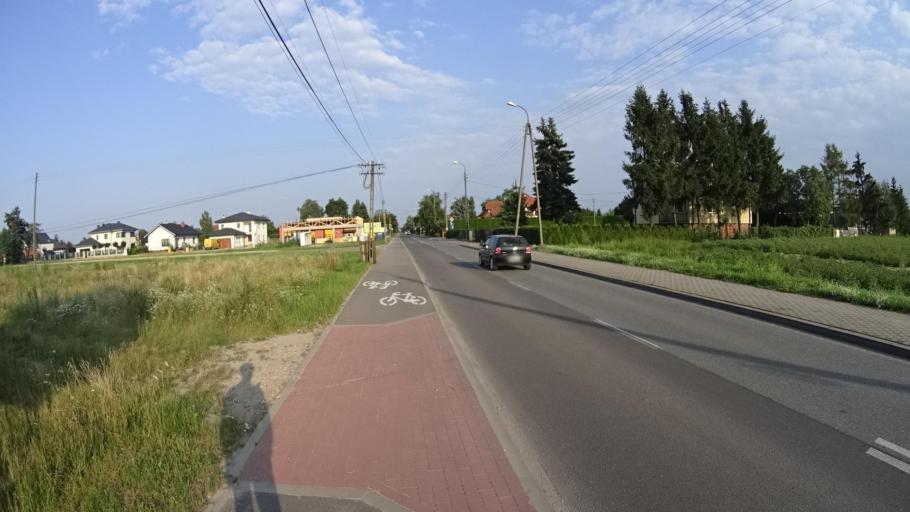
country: PL
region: Masovian Voivodeship
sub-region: Powiat pruszkowski
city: Rybie
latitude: 52.1488
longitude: 20.9401
